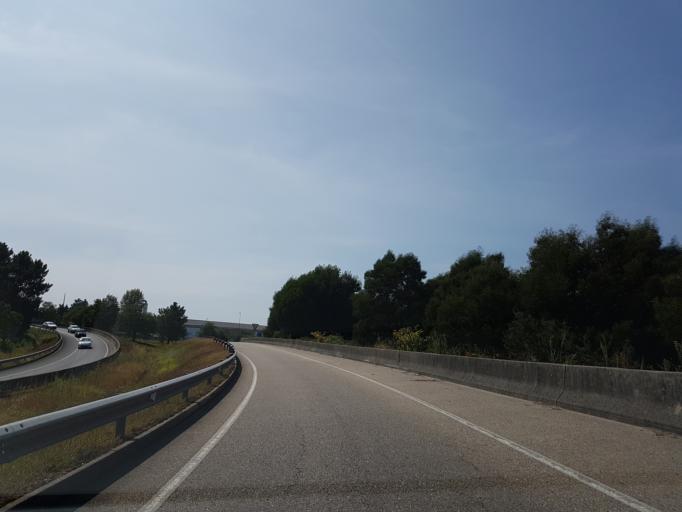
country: ES
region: Galicia
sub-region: Provincia de Pontevedra
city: Vigo
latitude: 42.2128
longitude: -8.6610
